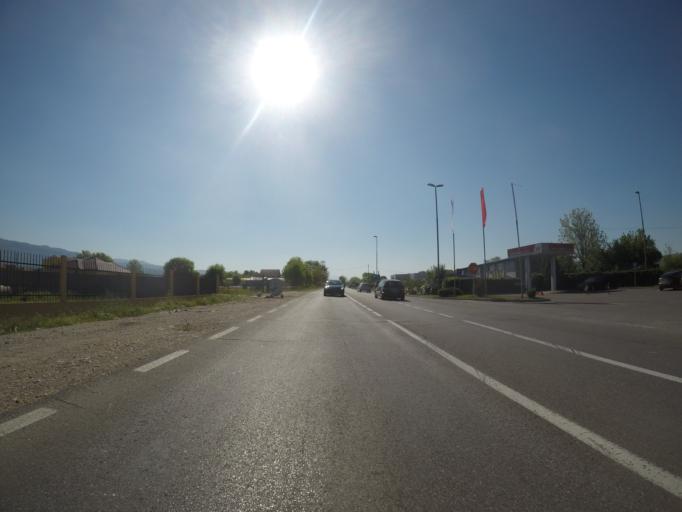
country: ME
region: Danilovgrad
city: Danilovgrad
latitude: 42.5447
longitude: 19.1043
